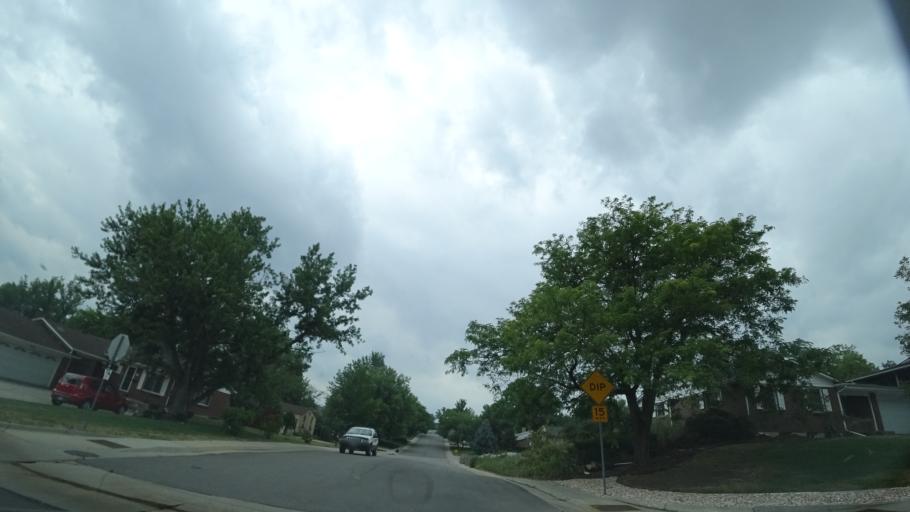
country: US
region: Colorado
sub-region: Jefferson County
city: West Pleasant View
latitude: 39.7025
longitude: -105.1497
